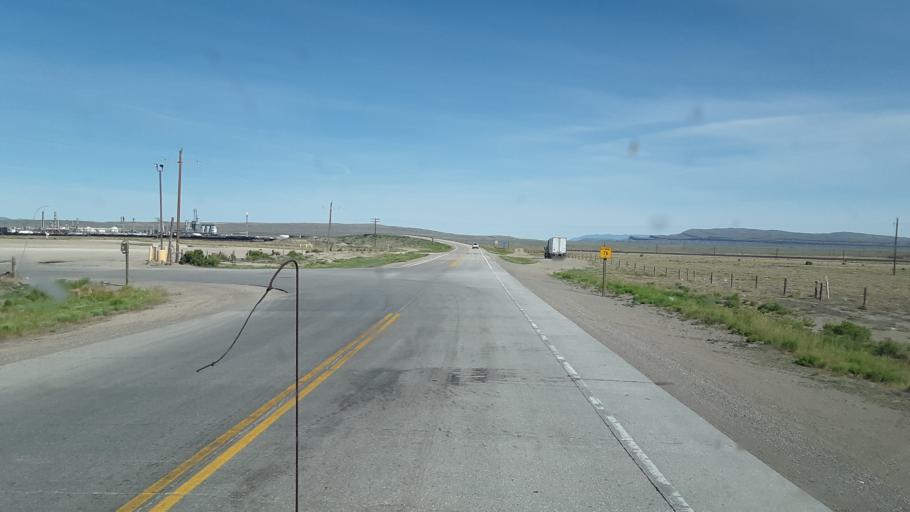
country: US
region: Wyoming
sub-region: Carbon County
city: Rawlins
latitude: 41.7737
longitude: -107.0833
